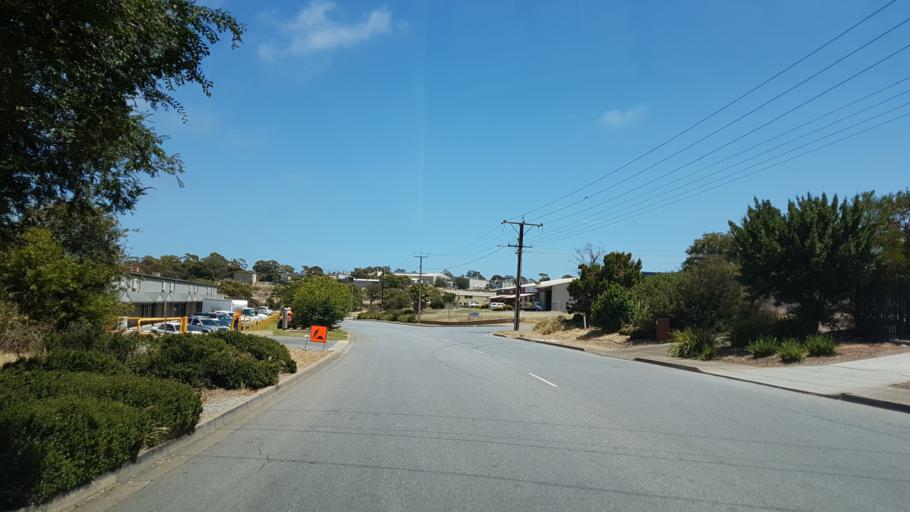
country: AU
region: South Australia
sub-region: Onkaparinga
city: Morphett Vale
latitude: -35.1119
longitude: 138.4966
